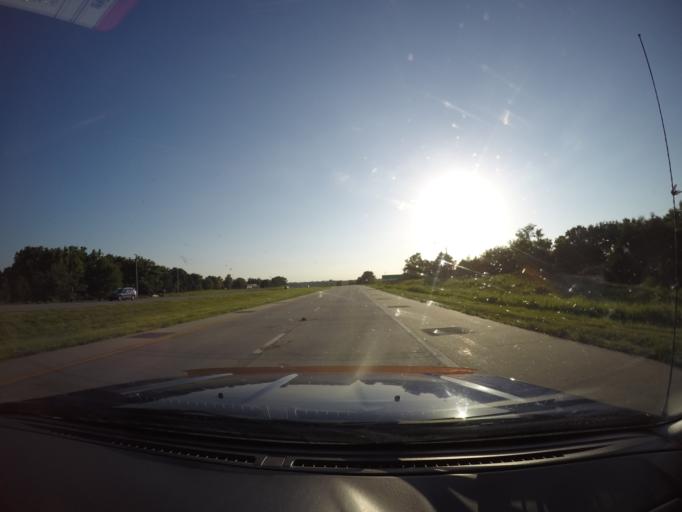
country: US
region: Kansas
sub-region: Pottawatomie County
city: Wamego
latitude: 39.2095
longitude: -96.4102
